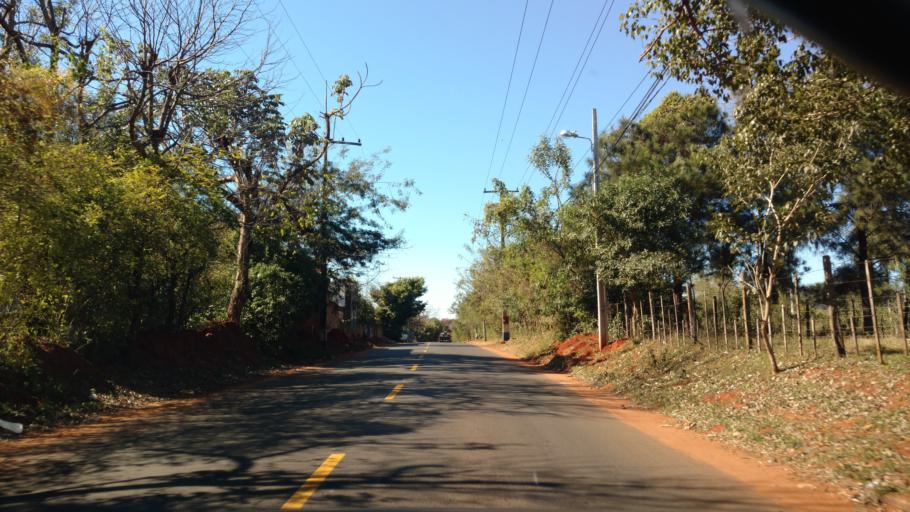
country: PY
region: Central
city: Itaugua
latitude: -25.3890
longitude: -57.3622
